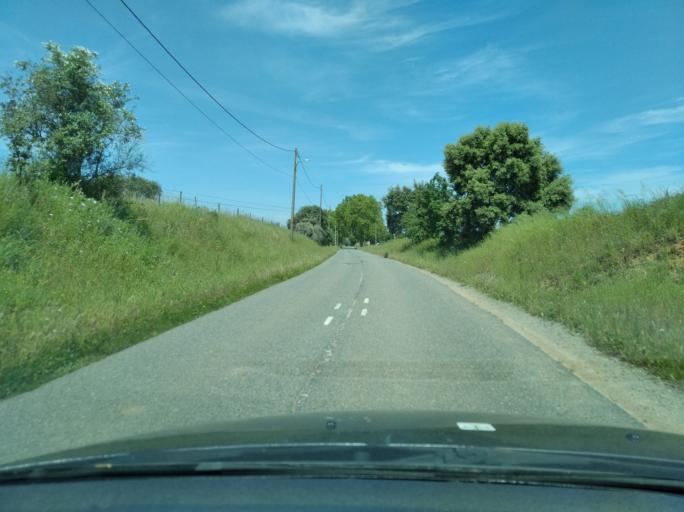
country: PT
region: Portalegre
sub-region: Avis
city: Avis
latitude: 39.0961
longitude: -7.8785
